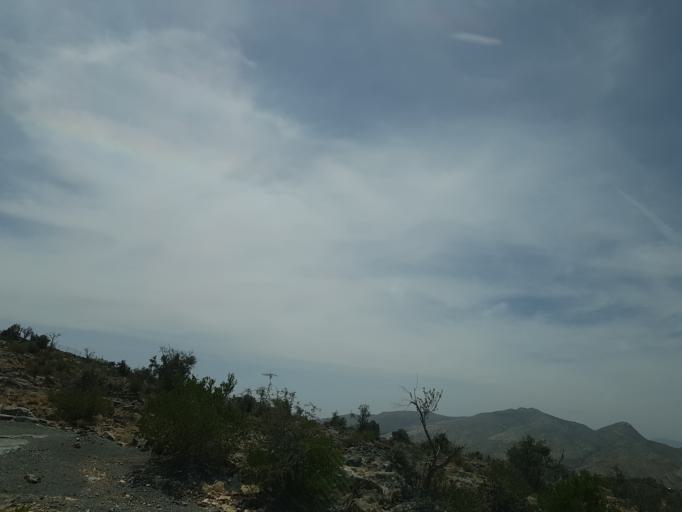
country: OM
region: Al Batinah
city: Bayt al `Awabi
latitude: 23.1412
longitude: 57.5374
